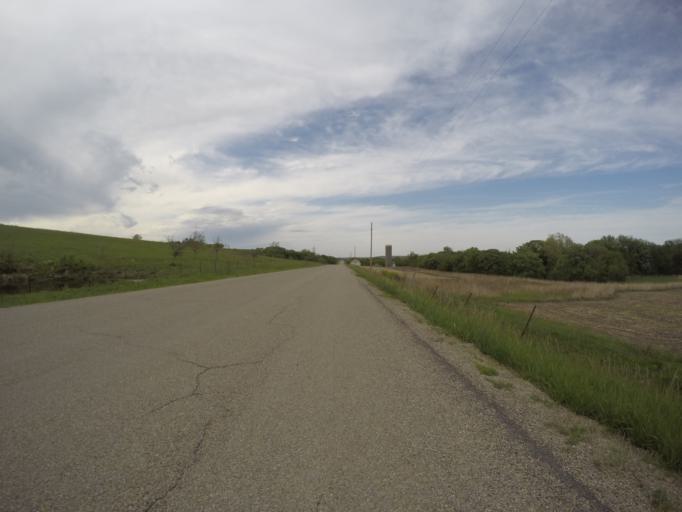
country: US
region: Kansas
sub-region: Riley County
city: Ogden
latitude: 39.0080
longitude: -96.6030
